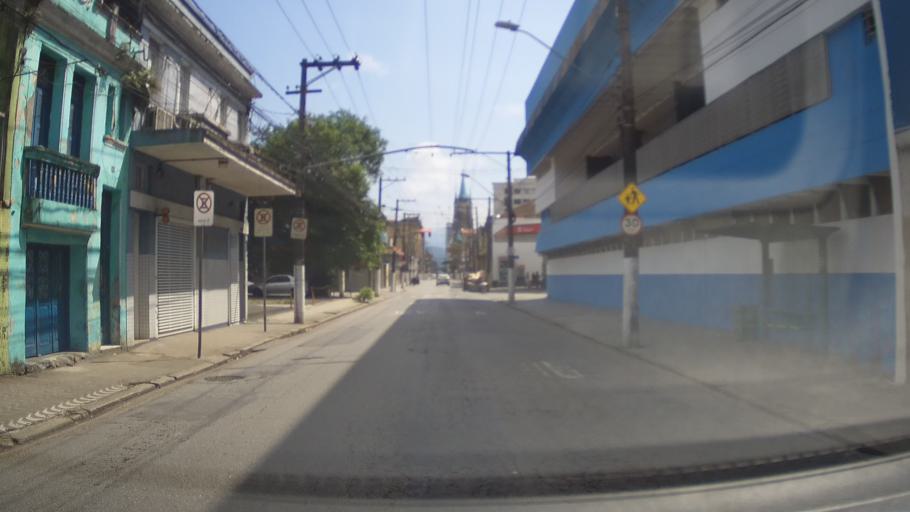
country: BR
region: Sao Paulo
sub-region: Santos
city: Santos
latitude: -23.9404
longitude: -46.3249
